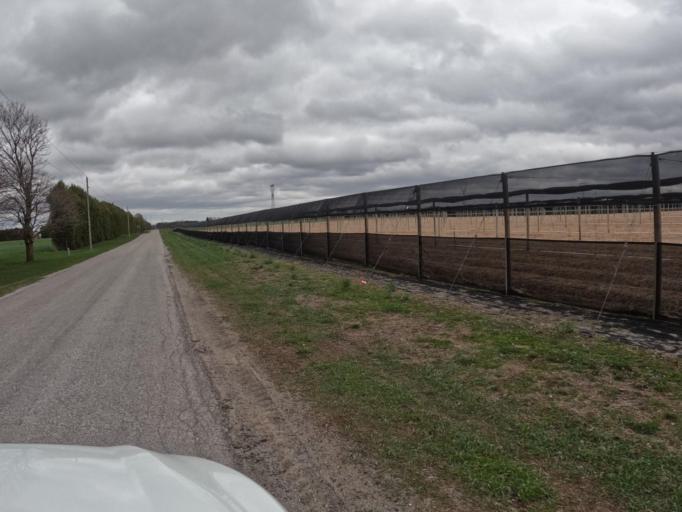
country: CA
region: Ontario
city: Norfolk County
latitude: 42.9639
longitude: -80.4283
